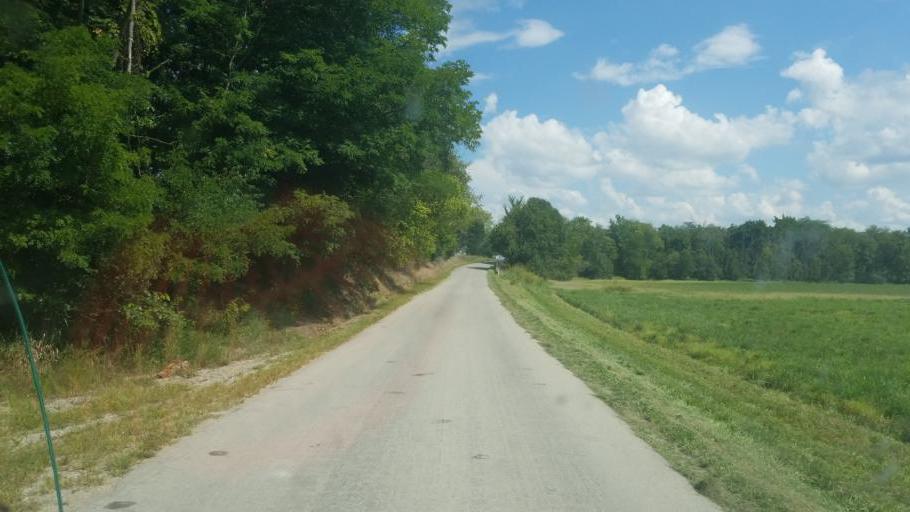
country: US
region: Ohio
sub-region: Wyandot County
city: Carey
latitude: 40.8758
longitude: -83.3676
